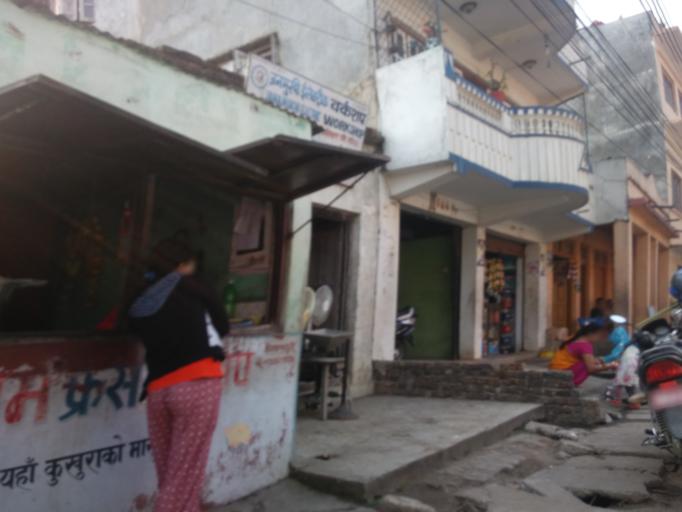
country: NP
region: Central Region
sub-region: Narayani Zone
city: Hitura
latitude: 27.4319
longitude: 85.0357
